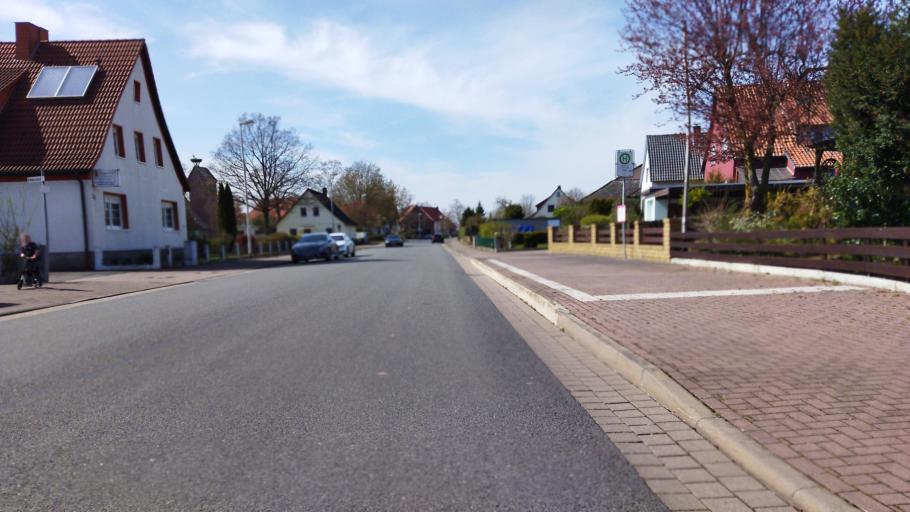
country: DE
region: Lower Saxony
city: Hameln
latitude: 52.1253
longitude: 9.3075
